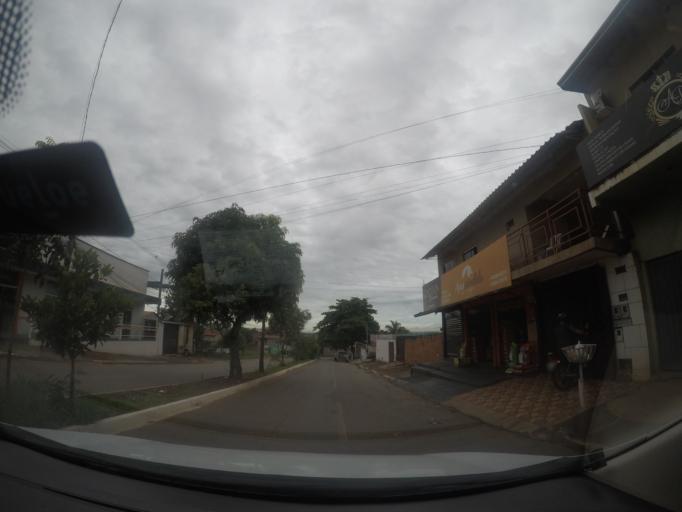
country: BR
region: Goias
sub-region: Goiania
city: Goiania
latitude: -16.6284
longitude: -49.3076
